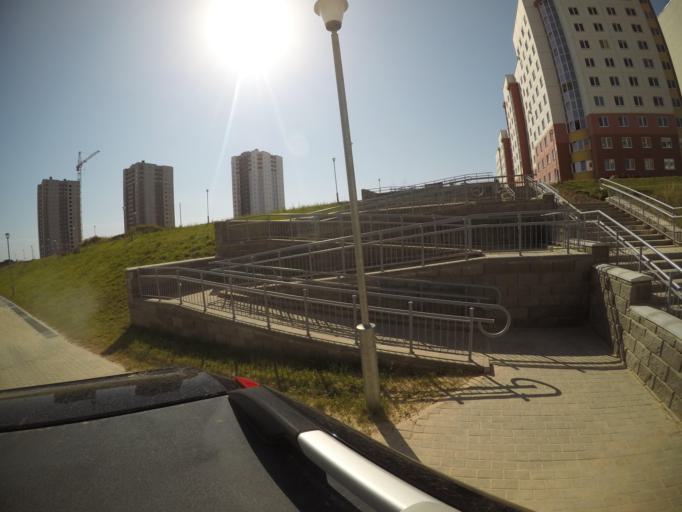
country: BY
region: Grodnenskaya
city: Hrodna
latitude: 53.7212
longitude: 23.8807
